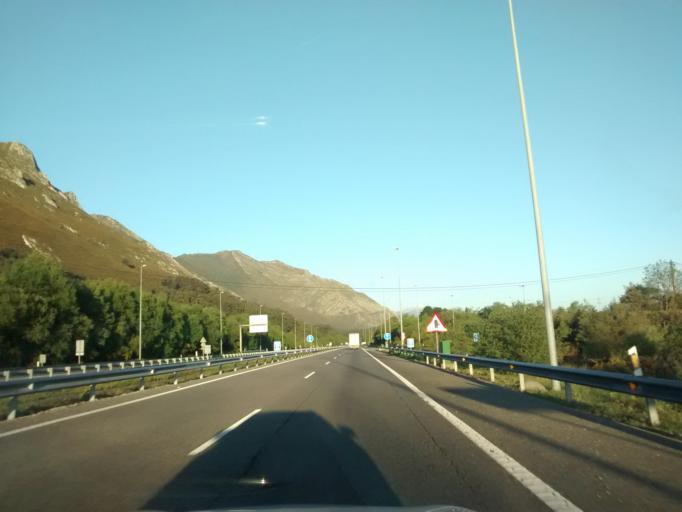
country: ES
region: Asturias
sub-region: Province of Asturias
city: Ribadesella
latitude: 43.4399
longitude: -4.9601
